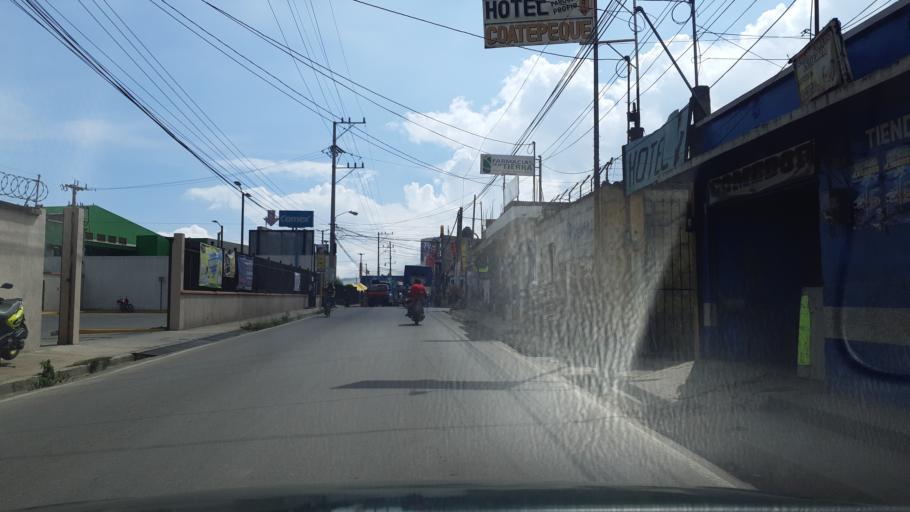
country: GT
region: Chimaltenango
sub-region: Municipio de Chimaltenango
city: Chimaltenango
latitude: 14.6617
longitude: -90.8111
